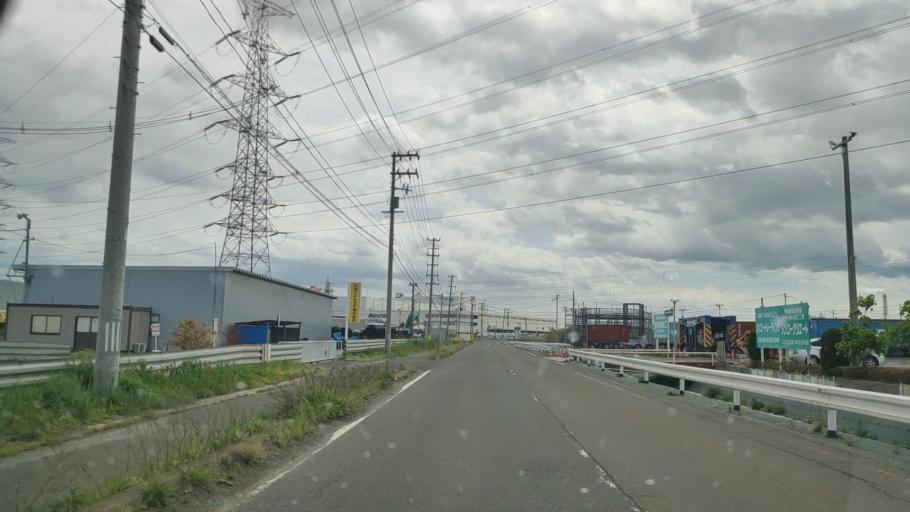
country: JP
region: Miyagi
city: Shiogama
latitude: 38.2789
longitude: 141.0092
